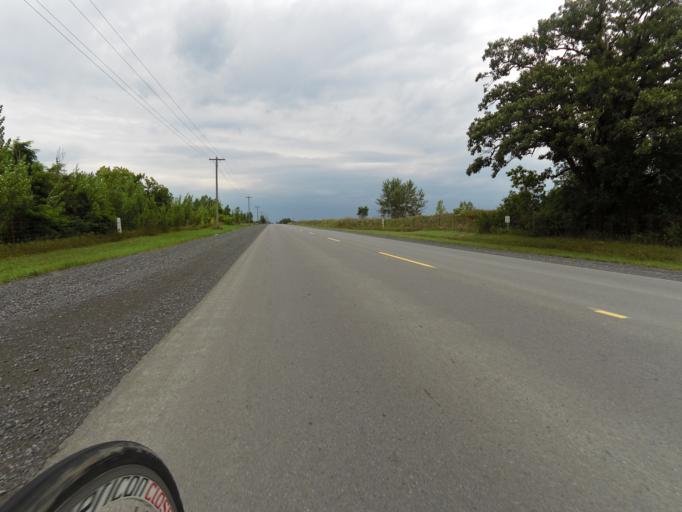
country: CA
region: Ontario
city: Bells Corners
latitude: 45.2289
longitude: -75.7792
